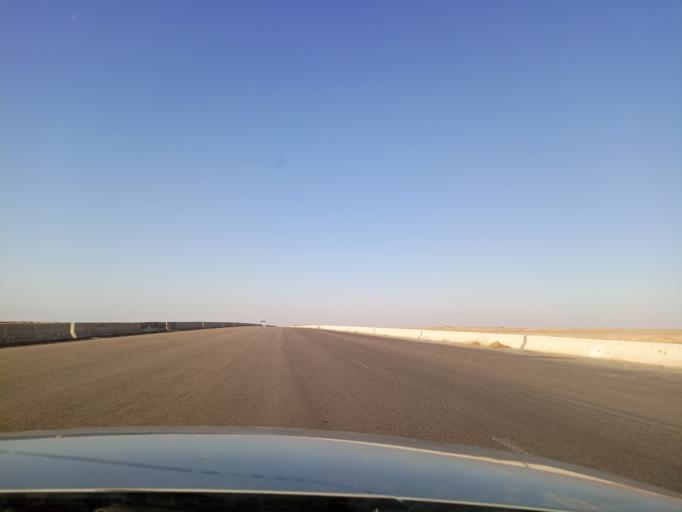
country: EG
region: Muhafazat al Fayyum
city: Tamiyah
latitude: 29.6217
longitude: 30.9492
